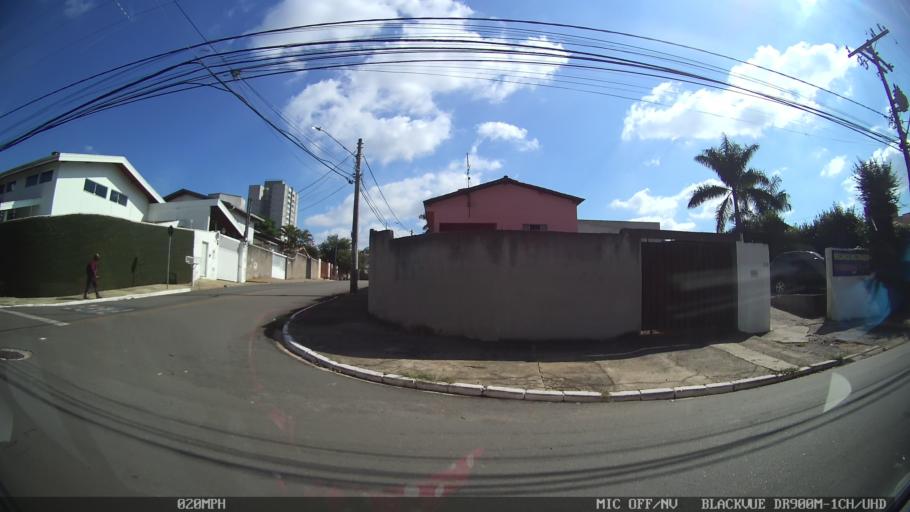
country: BR
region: Sao Paulo
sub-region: Hortolandia
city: Hortolandia
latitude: -22.8789
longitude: -47.2218
